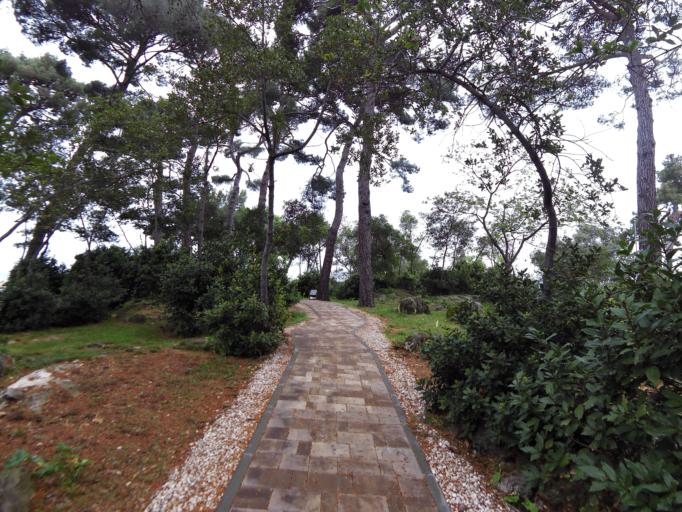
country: HR
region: Istarska
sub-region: Grad Porec
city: Porec
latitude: 45.2259
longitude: 13.5837
